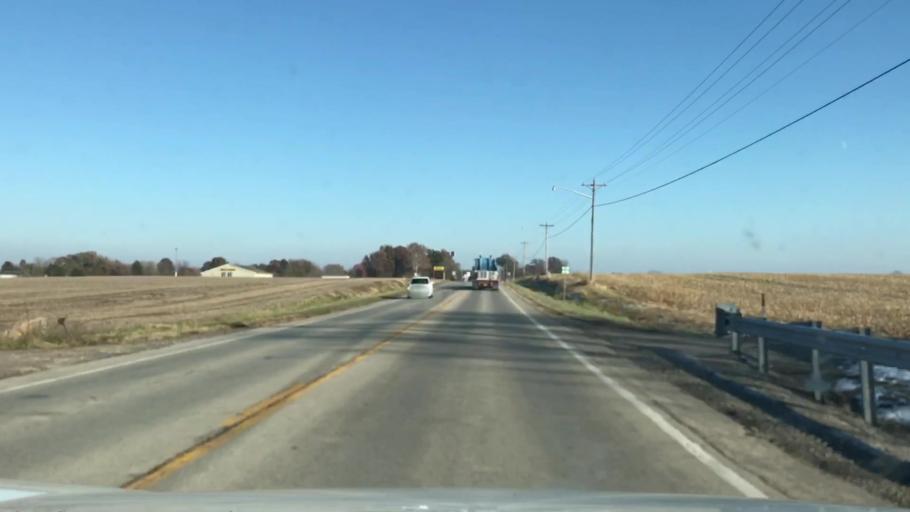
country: US
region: Illinois
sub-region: Clinton County
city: New Baden
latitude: 38.5353
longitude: -89.7189
